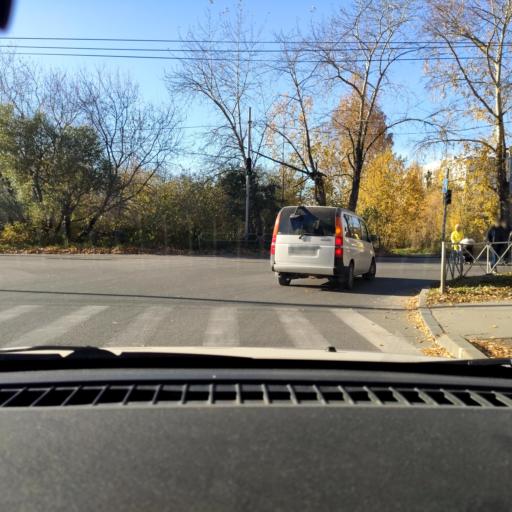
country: RU
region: Perm
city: Perm
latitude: 58.0638
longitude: 56.3543
